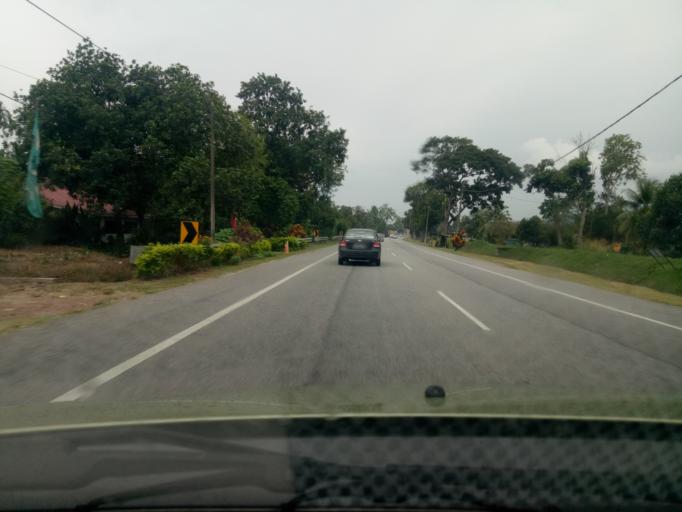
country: MY
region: Kedah
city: Gurun
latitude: 5.8714
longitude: 100.4521
